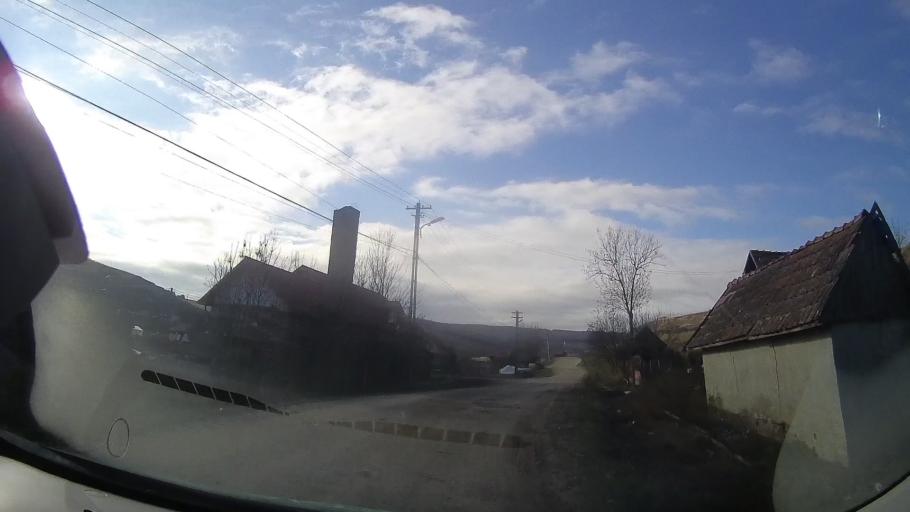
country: RO
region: Mures
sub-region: Comuna Papiu Ilarian
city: Papiu Ilarian
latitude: 46.5612
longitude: 24.2074
